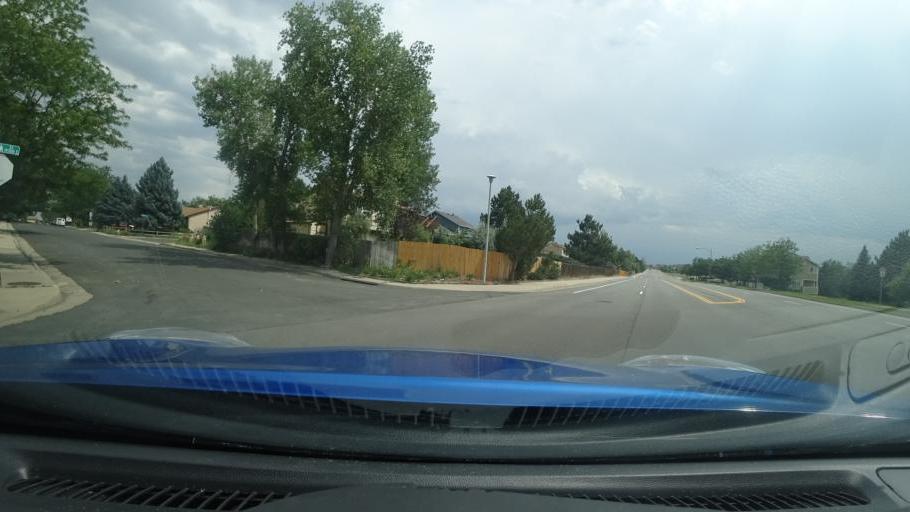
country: US
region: Colorado
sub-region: Adams County
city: Aurora
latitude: 39.6890
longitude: -104.7631
